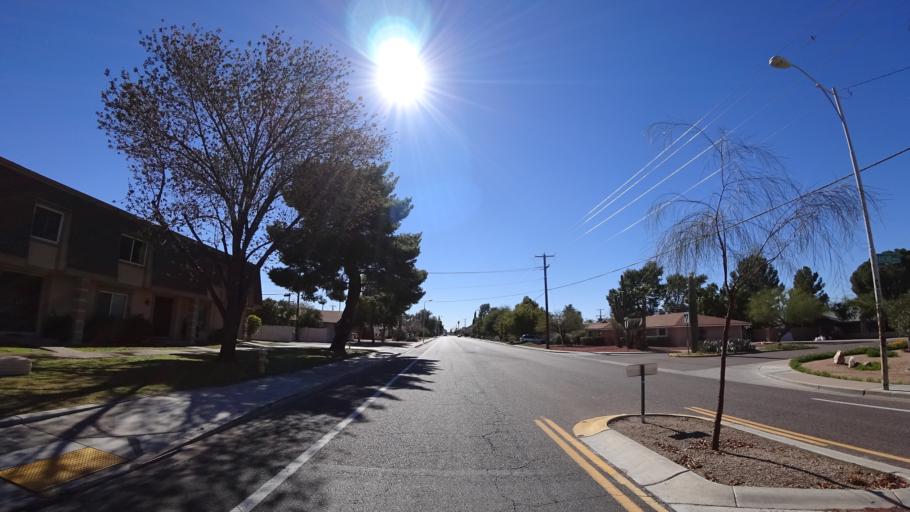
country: US
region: Arizona
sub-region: Maricopa County
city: Scottsdale
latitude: 33.5079
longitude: -111.9002
